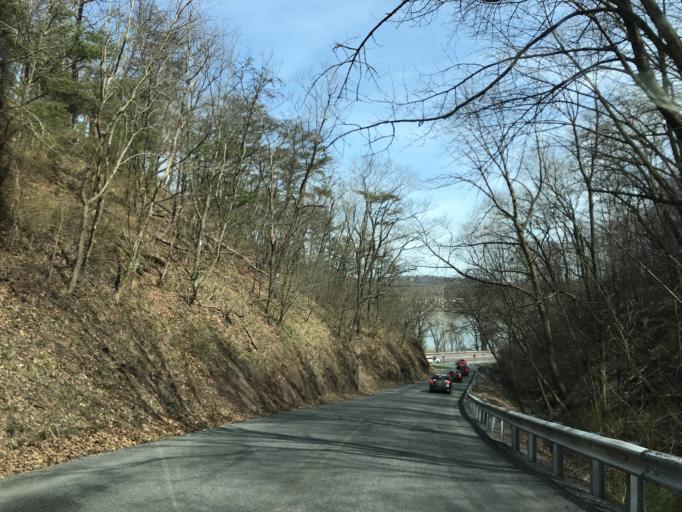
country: US
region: Pennsylvania
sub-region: Northumberland County
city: Northumberland
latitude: 40.8793
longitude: -76.8014
